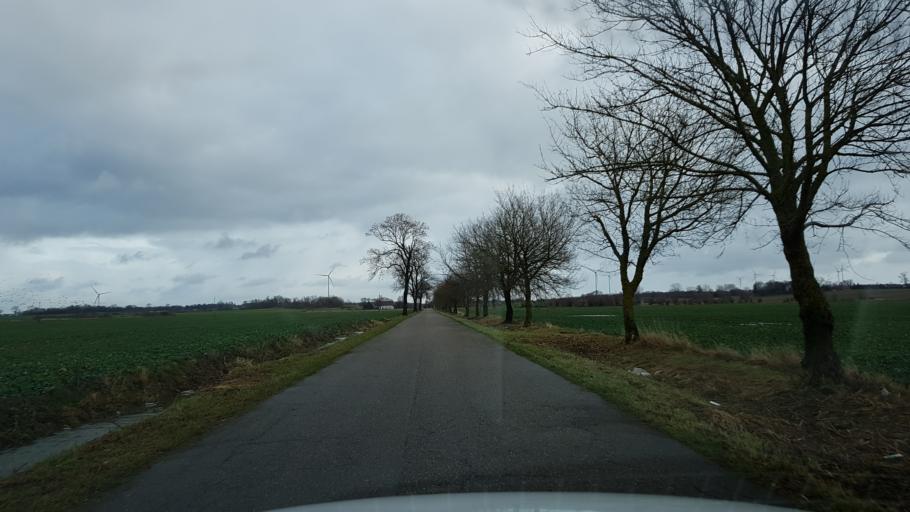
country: PL
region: West Pomeranian Voivodeship
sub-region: Powiat slawienski
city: Slawno
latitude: 54.5179
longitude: 16.6768
